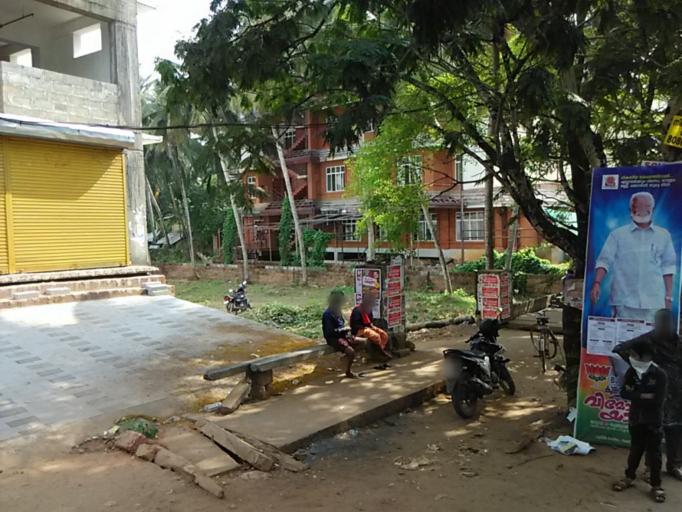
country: IN
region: Kerala
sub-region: Kozhikode
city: Kozhikode
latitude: 11.2585
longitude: 75.7952
